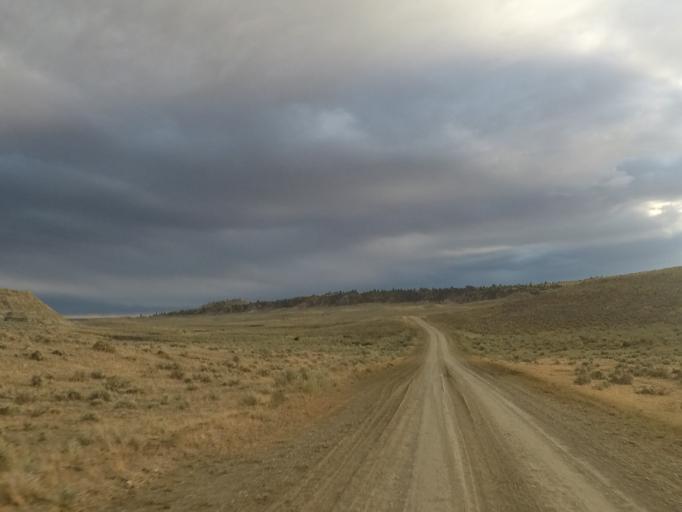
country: US
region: Montana
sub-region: Golden Valley County
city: Ryegate
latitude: 46.4450
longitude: -109.2575
